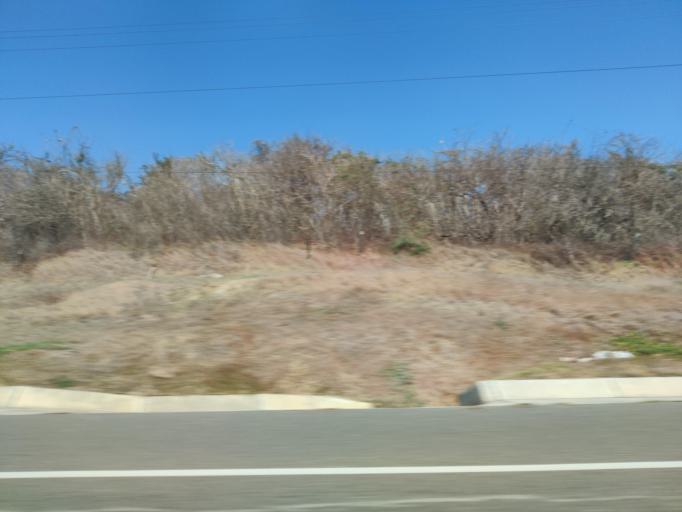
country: CO
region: Atlantico
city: Puerto Colombia
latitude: 10.9654
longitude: -74.9972
